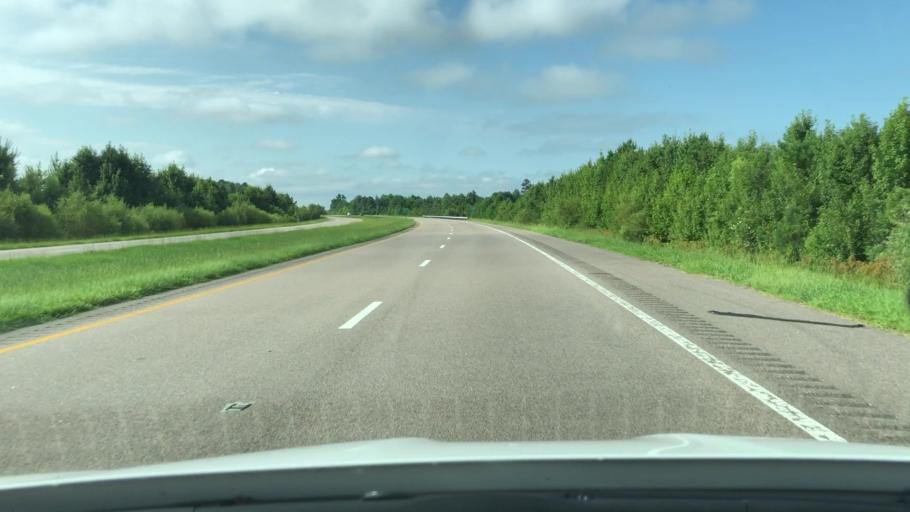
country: US
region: Virginia
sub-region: City of Portsmouth
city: Portsmouth Heights
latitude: 36.6045
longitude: -76.3802
